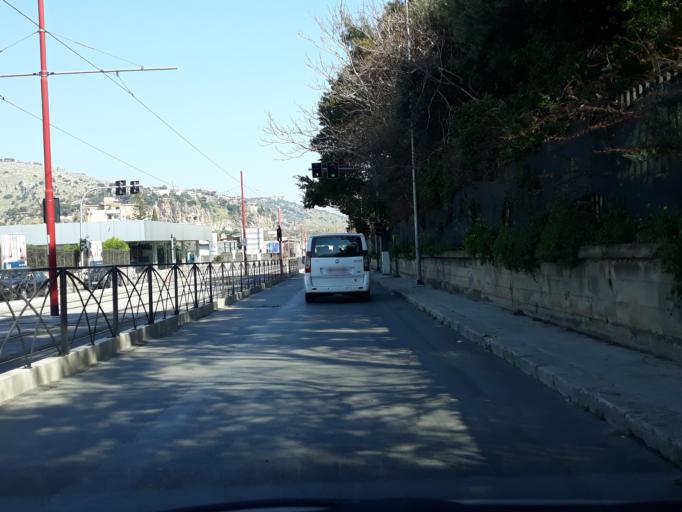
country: IT
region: Sicily
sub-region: Palermo
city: Palermo
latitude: 38.1282
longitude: 13.3028
